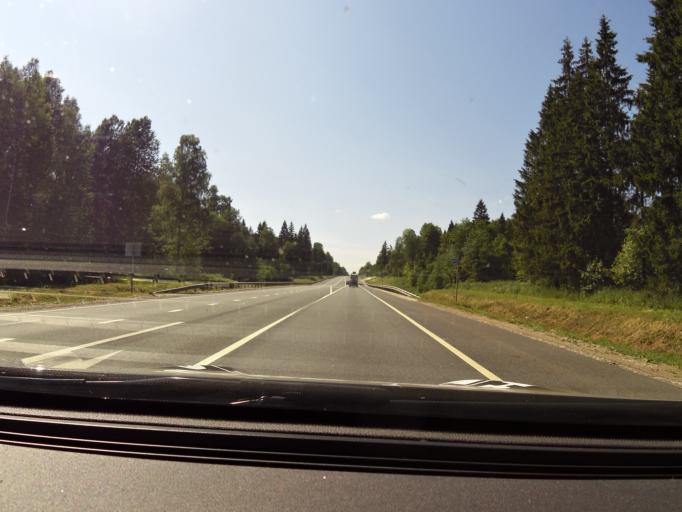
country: RU
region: Novgorod
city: Kresttsy
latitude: 58.3672
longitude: 32.1348
